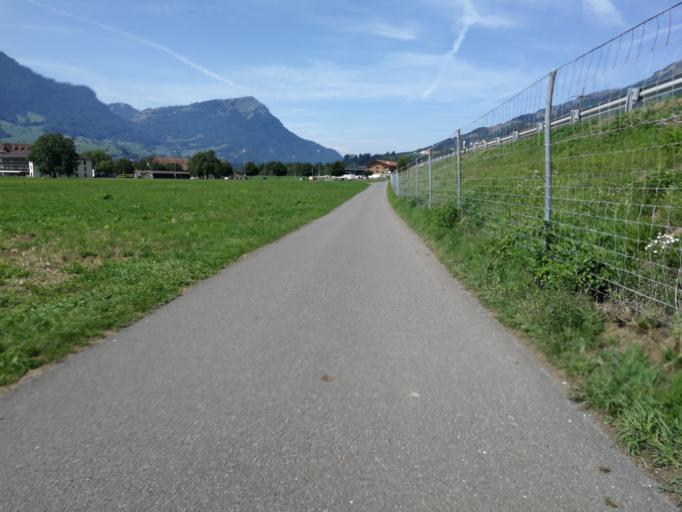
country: CH
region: Schwyz
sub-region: Bezirk Schwyz
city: Steinen
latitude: 47.0405
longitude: 8.6092
